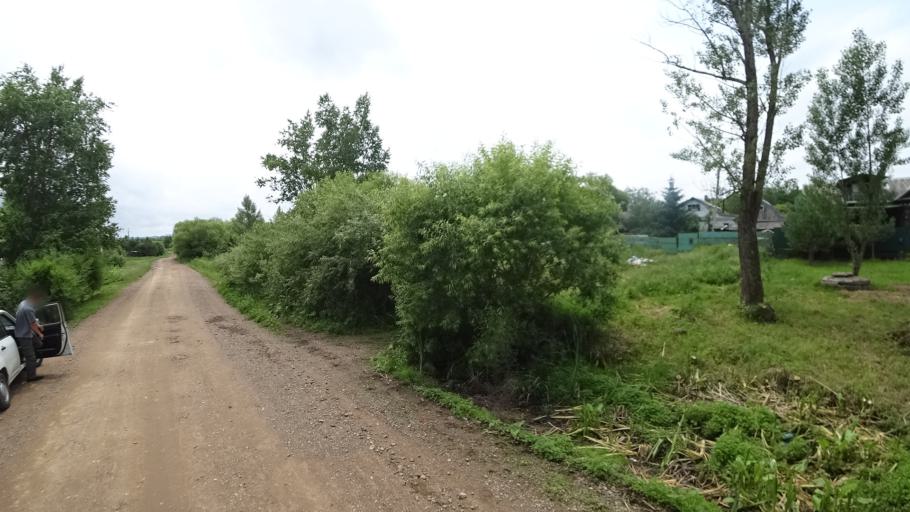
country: RU
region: Primorskiy
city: Novosysoyevka
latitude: 44.2283
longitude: 133.3671
